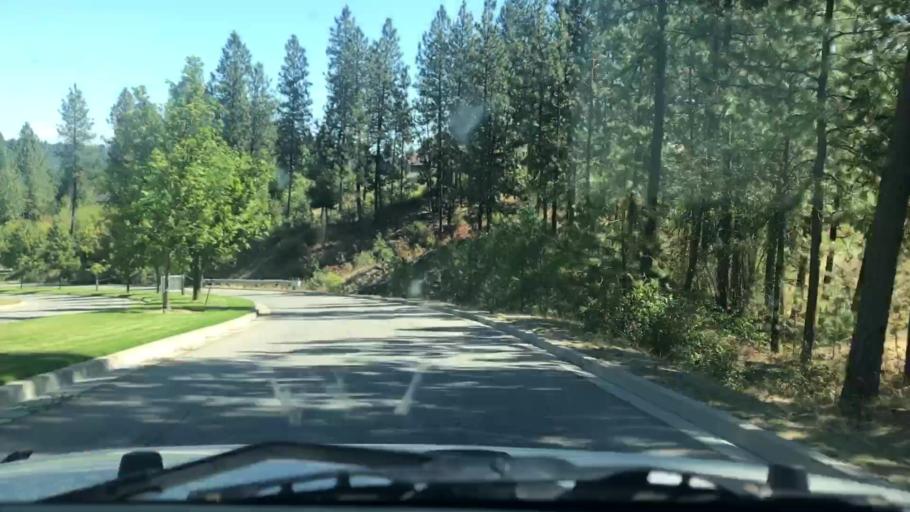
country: US
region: Washington
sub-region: Spokane County
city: Spokane
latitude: 47.5940
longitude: -117.4206
